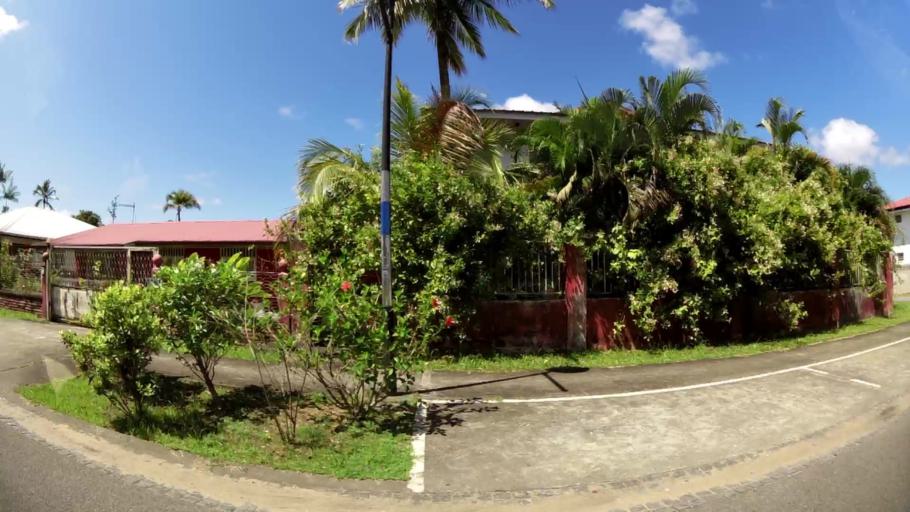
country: GF
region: Guyane
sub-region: Guyane
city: Matoury
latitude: 4.8496
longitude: -52.3286
